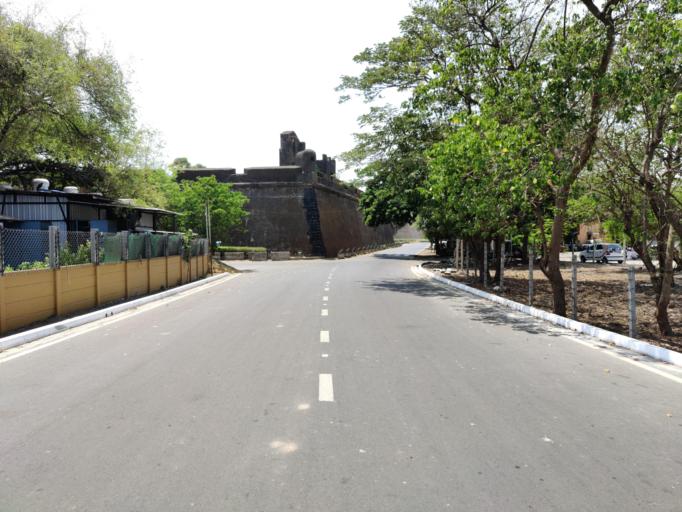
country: IN
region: Daman and Diu
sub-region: Daman District
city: Daman
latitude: 20.4069
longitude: 72.8292
